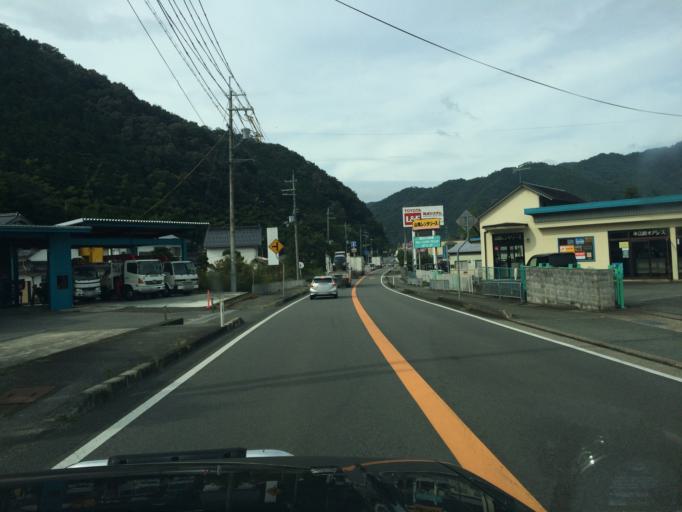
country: JP
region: Hyogo
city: Toyooka
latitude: 35.3492
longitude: 134.8363
